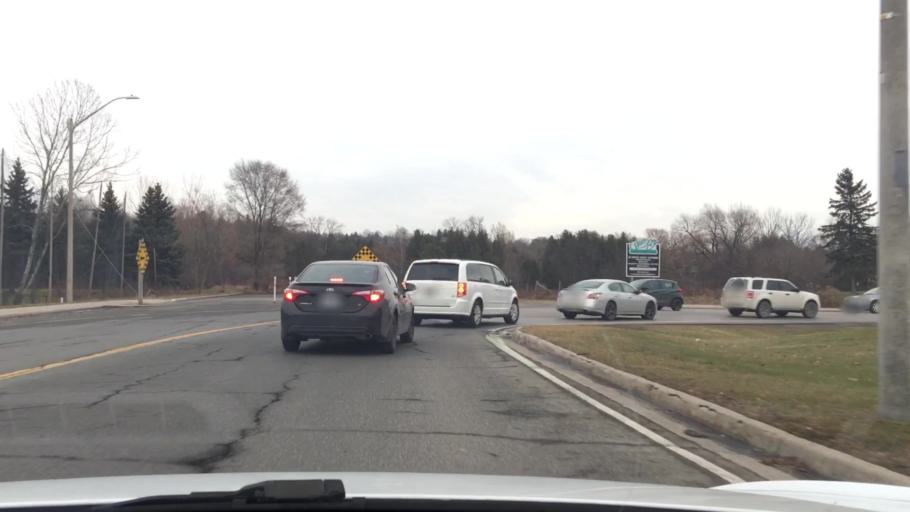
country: CA
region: Ontario
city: Oshawa
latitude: 43.8890
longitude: -78.8240
